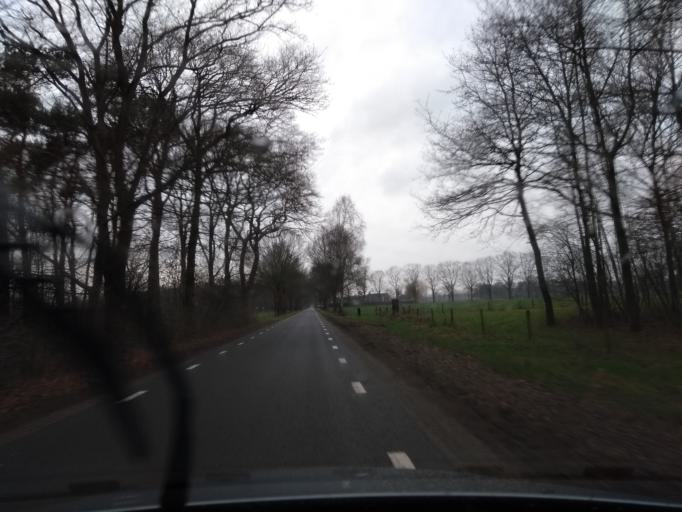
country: NL
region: Gelderland
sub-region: Gemeente Bronckhorst
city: Zelhem
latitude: 52.0350
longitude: 6.3427
